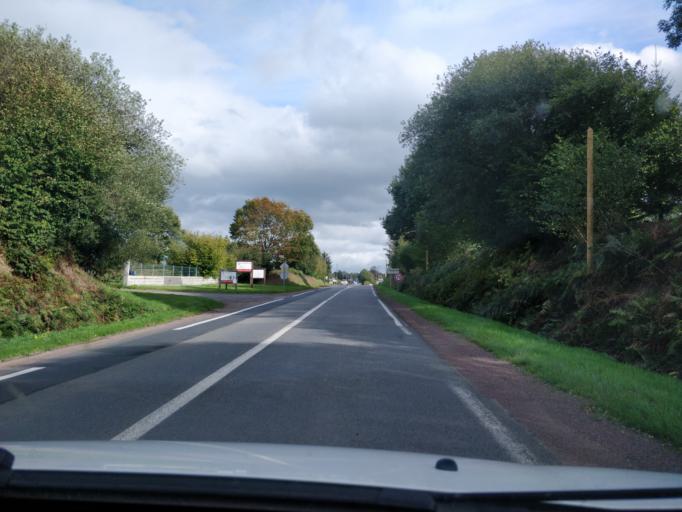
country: FR
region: Lower Normandy
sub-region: Departement du Calvados
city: Saint-Sever-Calvados
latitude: 48.8403
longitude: -0.9895
